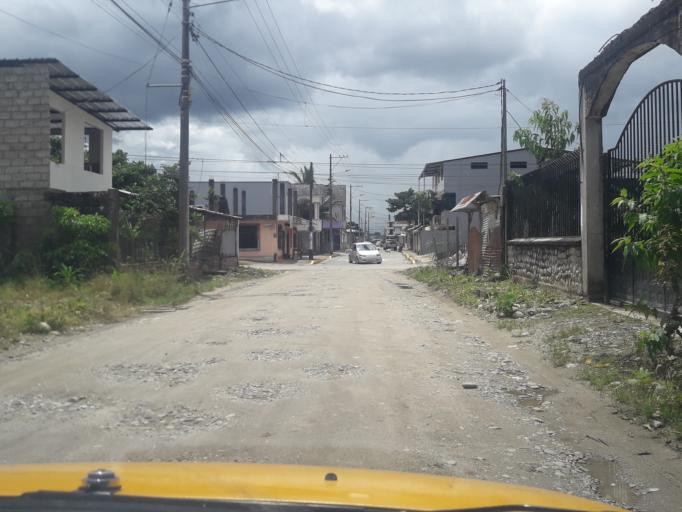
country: EC
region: Napo
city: Tena
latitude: -1.0083
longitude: -77.8155
